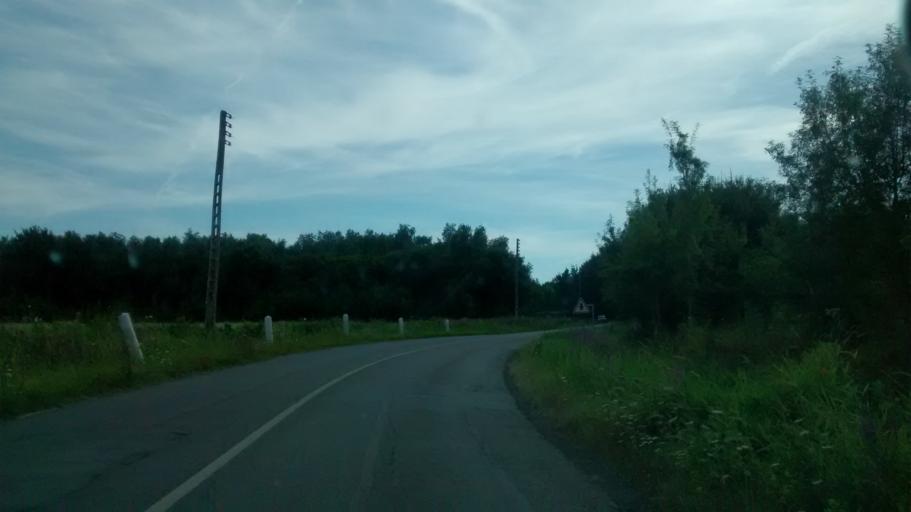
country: FR
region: Pays de la Loire
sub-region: Departement de la Loire-Atlantique
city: Pont-Saint-Martin
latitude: 47.1352
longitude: -1.6113
